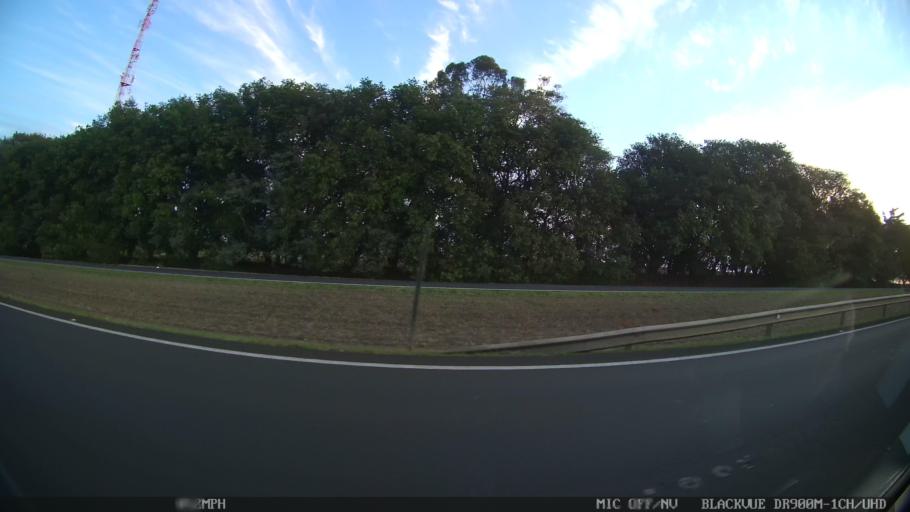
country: BR
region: Sao Paulo
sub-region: Catanduva
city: Catanduva
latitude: -21.1725
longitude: -48.9701
